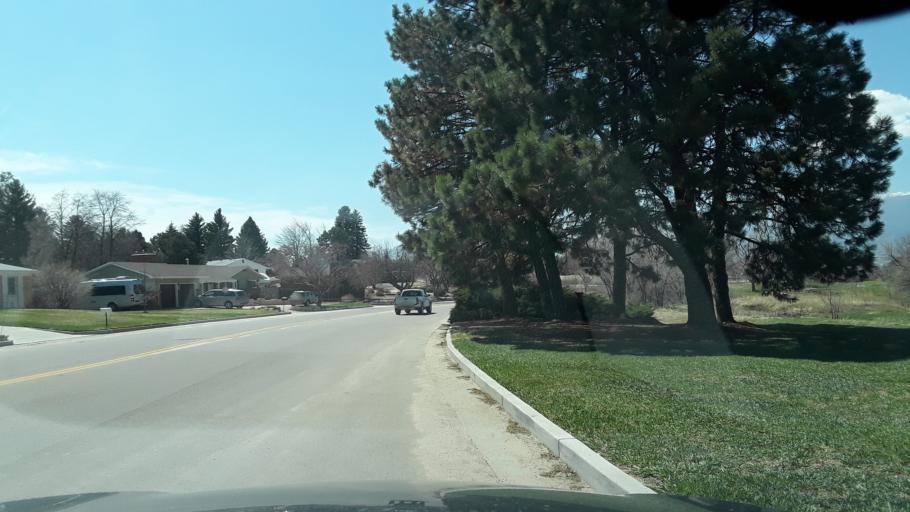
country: US
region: Colorado
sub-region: El Paso County
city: Colorado Springs
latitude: 38.8766
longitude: -104.7859
